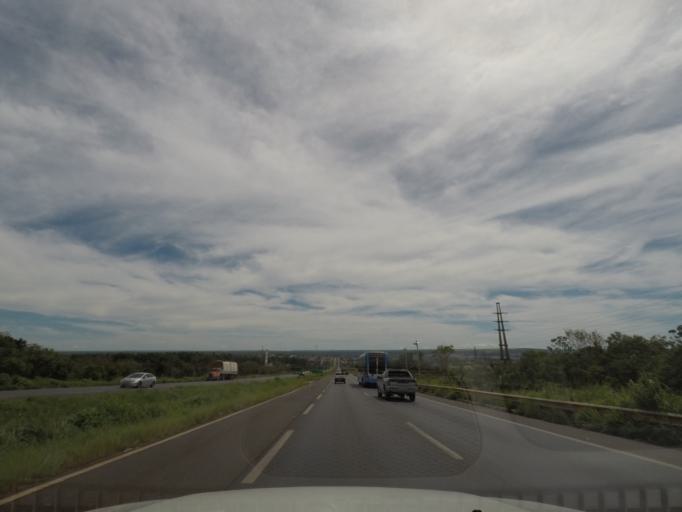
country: BR
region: Goias
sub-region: Planaltina
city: Planaltina
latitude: -15.6167
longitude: -47.7087
